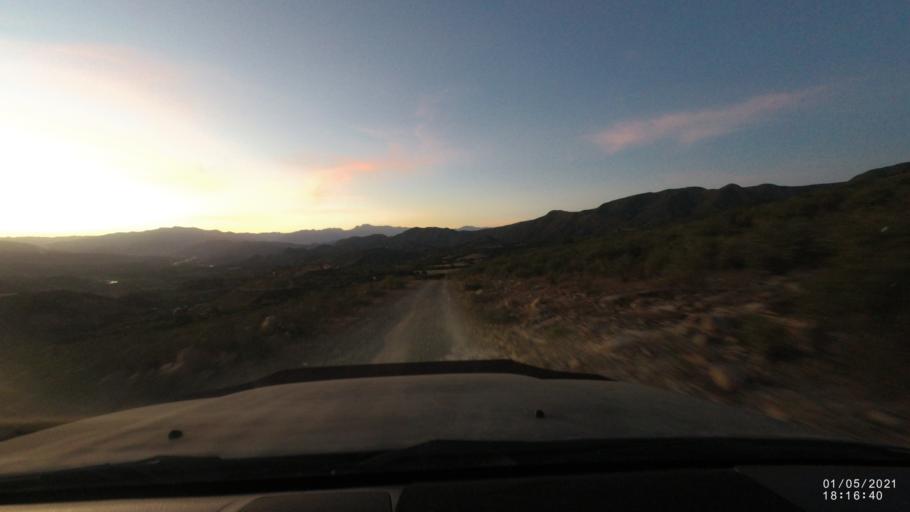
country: BO
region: Cochabamba
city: Capinota
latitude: -17.6705
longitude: -66.2179
